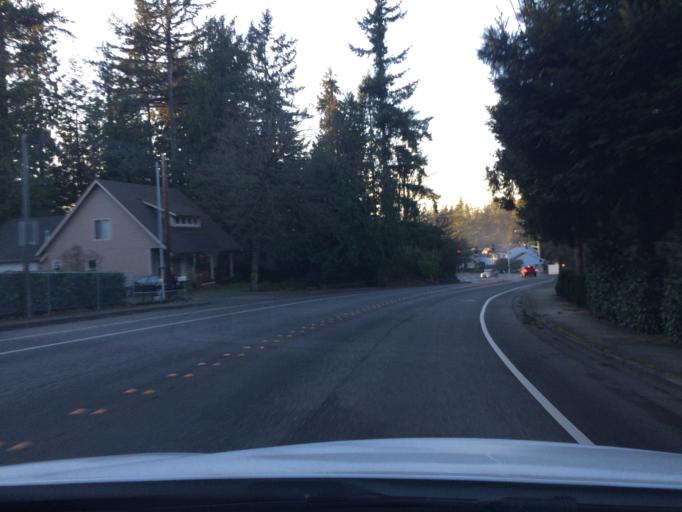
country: US
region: Washington
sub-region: Whatcom County
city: Geneva
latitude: 48.7482
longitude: -122.4243
